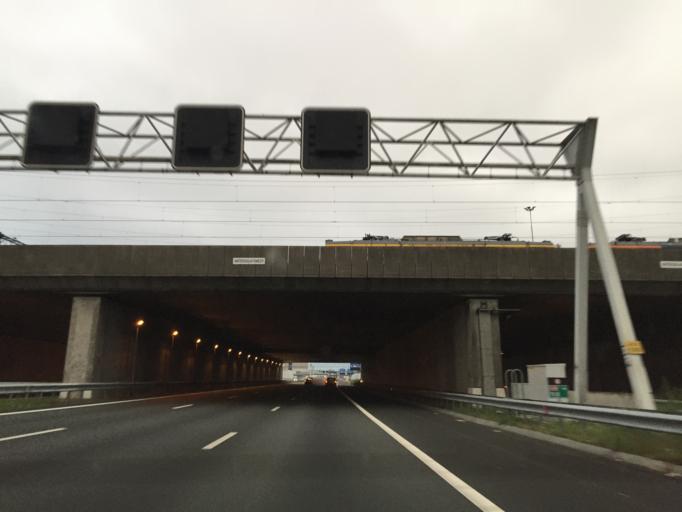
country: NL
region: North Holland
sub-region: Gemeente Diemen
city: Diemen
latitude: 52.3492
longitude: 4.9609
